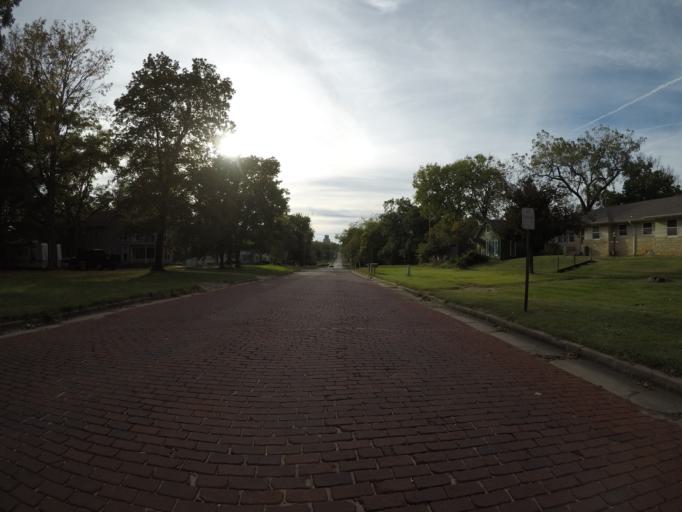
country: US
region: Kansas
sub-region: Douglas County
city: Baldwin City
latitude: 38.7749
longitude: -95.1909
